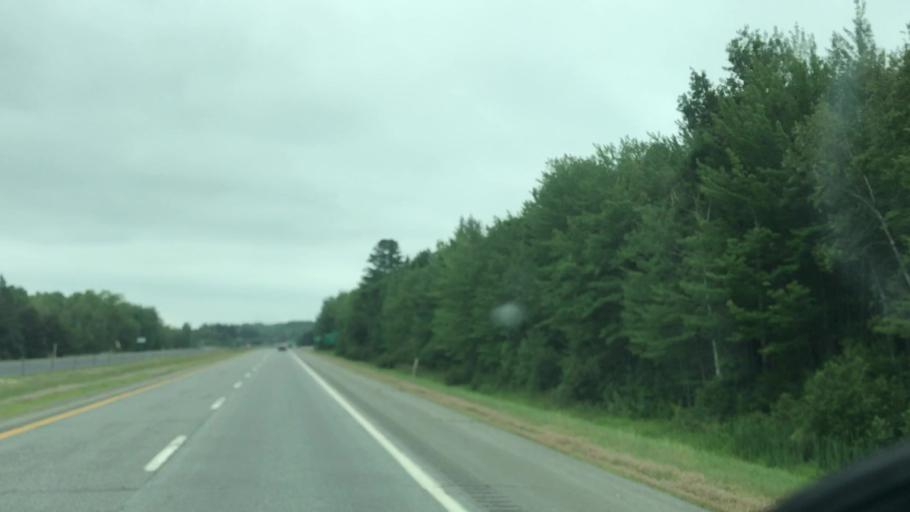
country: US
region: Maine
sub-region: Penobscot County
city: Orono
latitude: 44.9091
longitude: -68.6953
